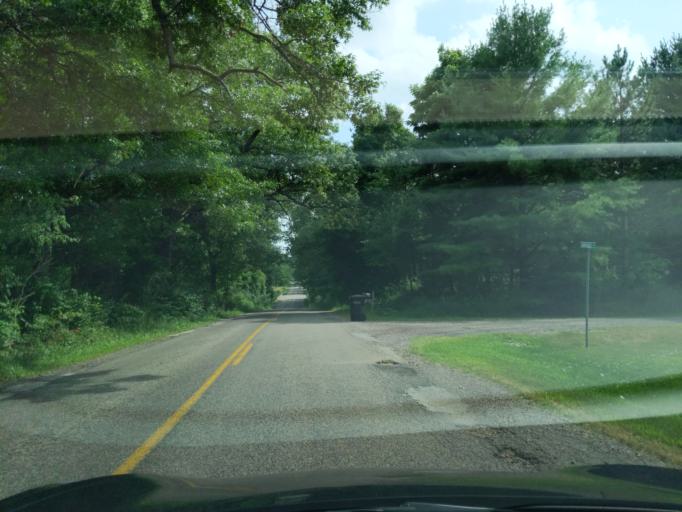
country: US
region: Michigan
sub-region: Eaton County
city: Eaton Rapids
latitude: 42.5015
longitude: -84.6307
